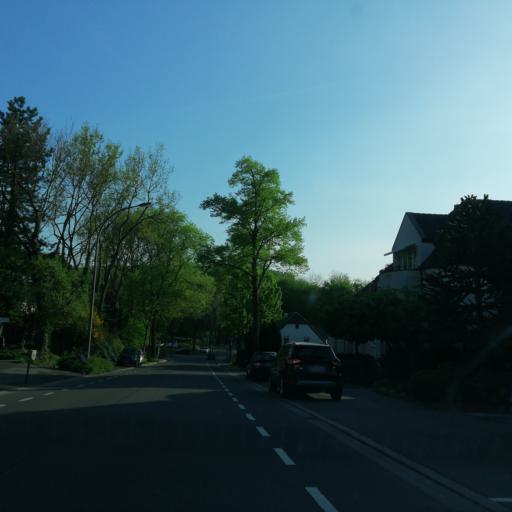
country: DE
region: North Rhine-Westphalia
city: Herdecke
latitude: 51.4467
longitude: 7.4572
